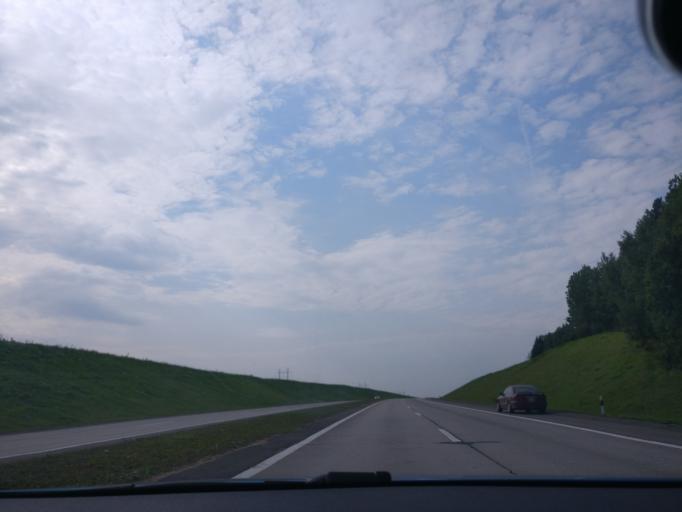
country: BY
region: Minsk
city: Astrashytski Haradok
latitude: 54.1029
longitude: 27.7954
